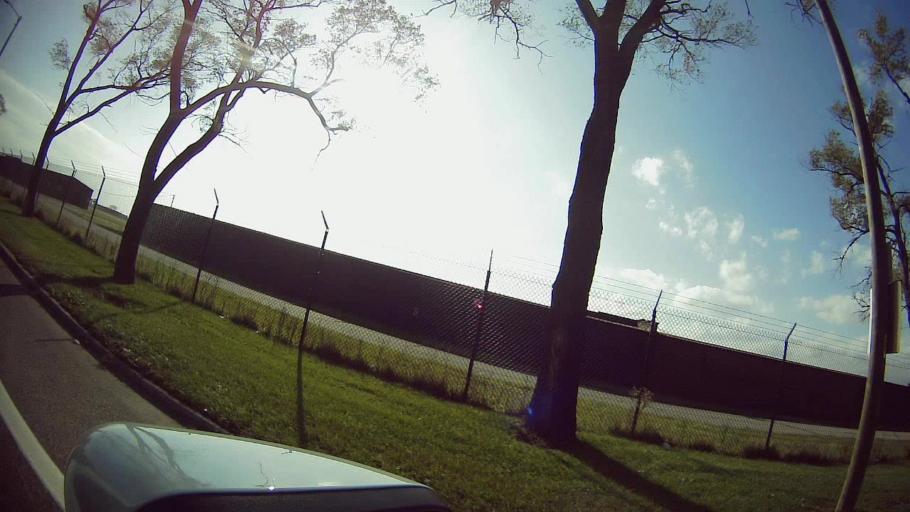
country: US
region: Michigan
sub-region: Wayne County
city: Hamtramck
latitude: 42.4162
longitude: -83.0104
